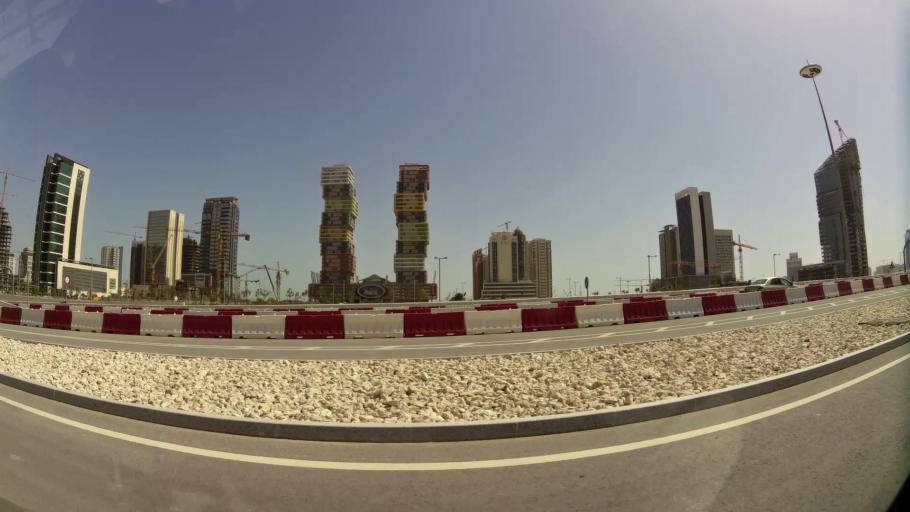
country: QA
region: Baladiyat ad Dawhah
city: Doha
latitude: 25.3853
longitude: 51.5194
